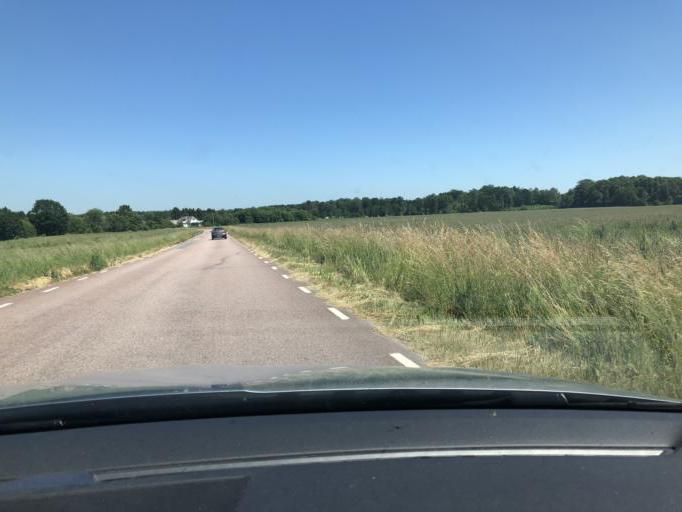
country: SE
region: Blekinge
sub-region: Olofstroms Kommun
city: Jamshog
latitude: 56.1772
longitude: 14.6098
